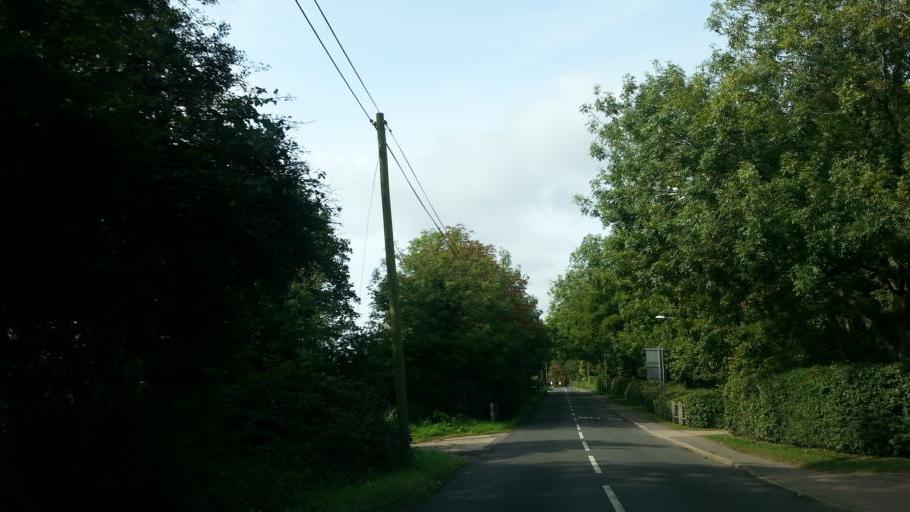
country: GB
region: England
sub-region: Cambridgeshire
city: Comberton
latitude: 52.2100
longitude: 0.0114
